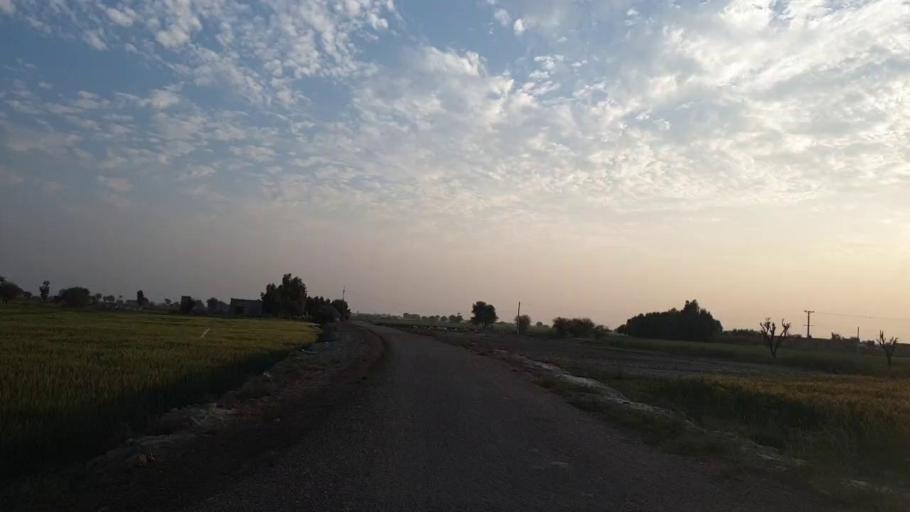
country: PK
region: Sindh
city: Pithoro
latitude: 25.5877
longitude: 69.3045
